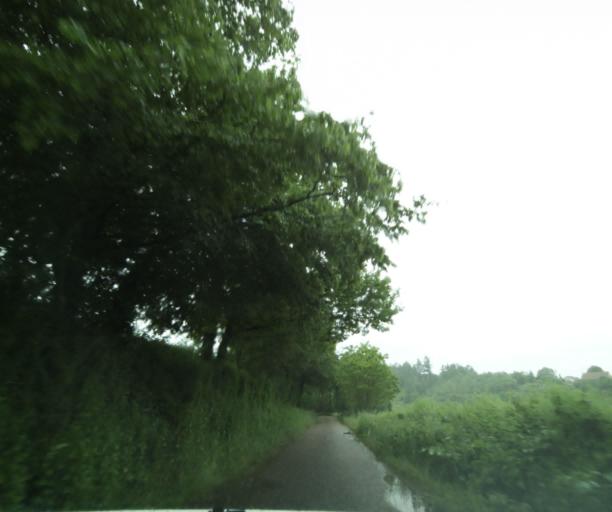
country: FR
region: Bourgogne
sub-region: Departement de Saone-et-Loire
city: Charolles
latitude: 46.3911
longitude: 4.3313
